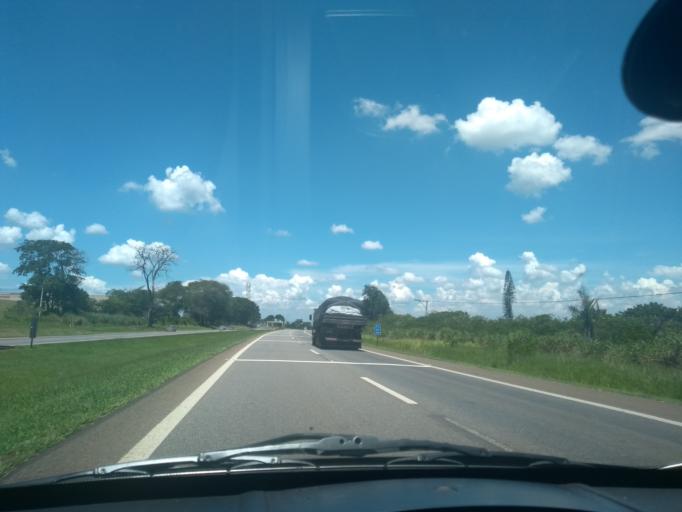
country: BR
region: Sao Paulo
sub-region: Mogi-Mirim
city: Mogi Mirim
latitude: -22.4872
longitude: -46.9812
